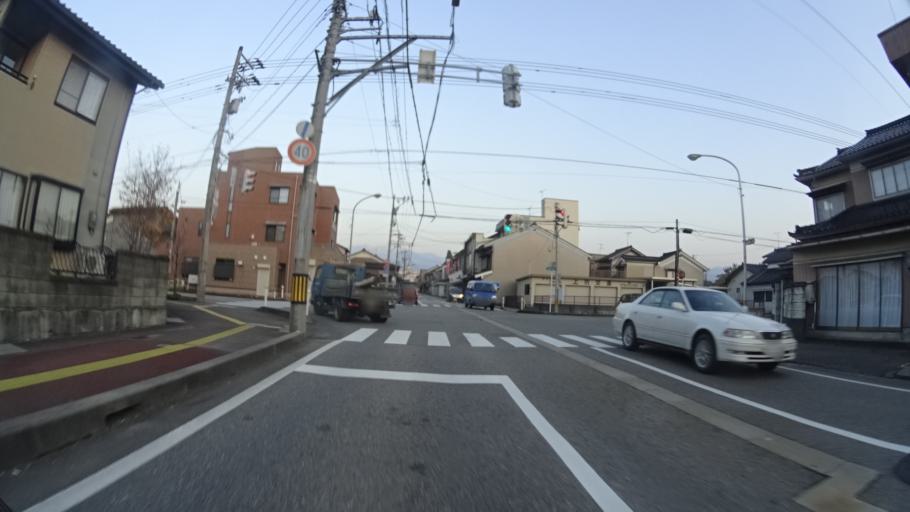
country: JP
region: Toyama
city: Kamiichi
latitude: 36.7065
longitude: 137.3587
